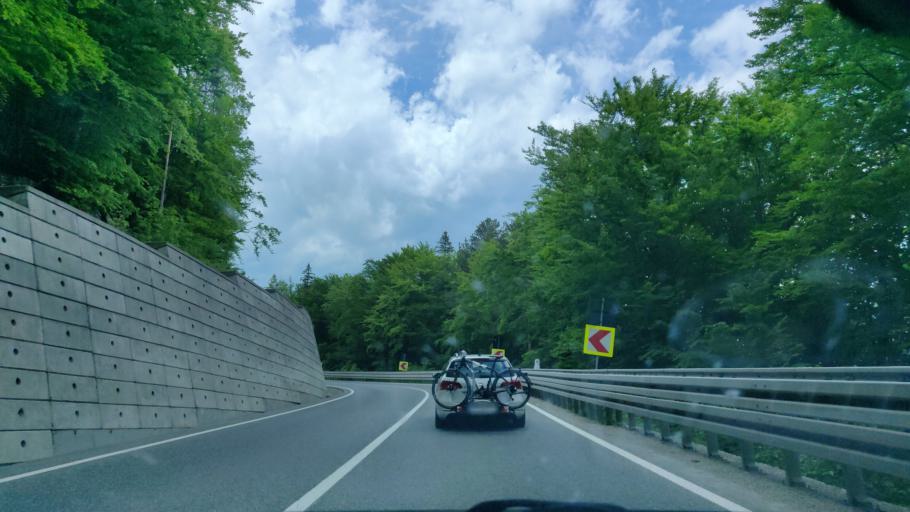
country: RO
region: Vrancea
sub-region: Comuna Tulnici
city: Tulnici
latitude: 45.9188
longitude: 26.6629
